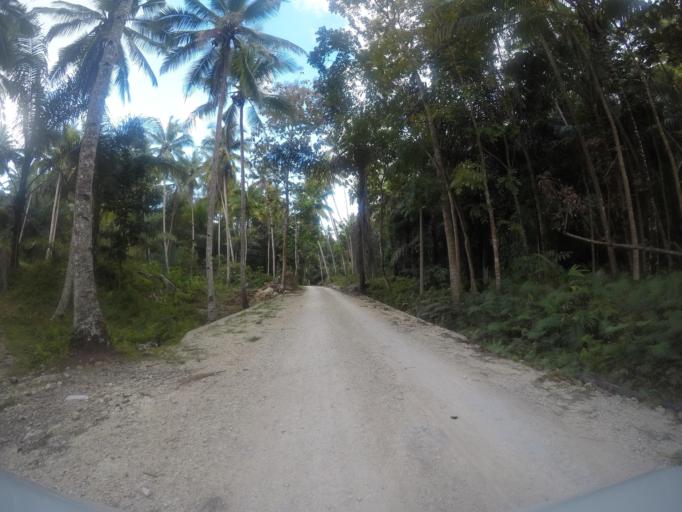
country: TL
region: Lautem
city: Lospalos
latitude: -8.5272
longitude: 126.9355
